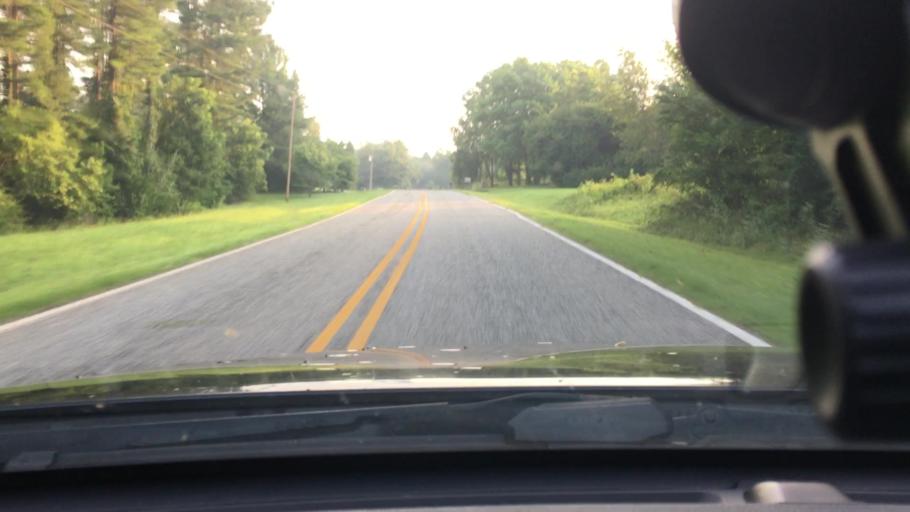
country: US
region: North Carolina
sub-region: Rutherford County
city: Rutherfordton
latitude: 35.3812
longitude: -81.9864
